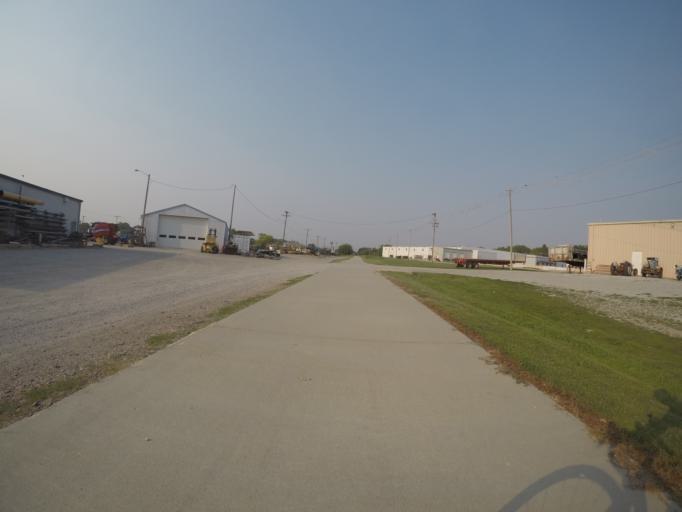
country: US
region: Nebraska
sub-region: Gage County
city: Beatrice
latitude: 40.2815
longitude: -96.7460
